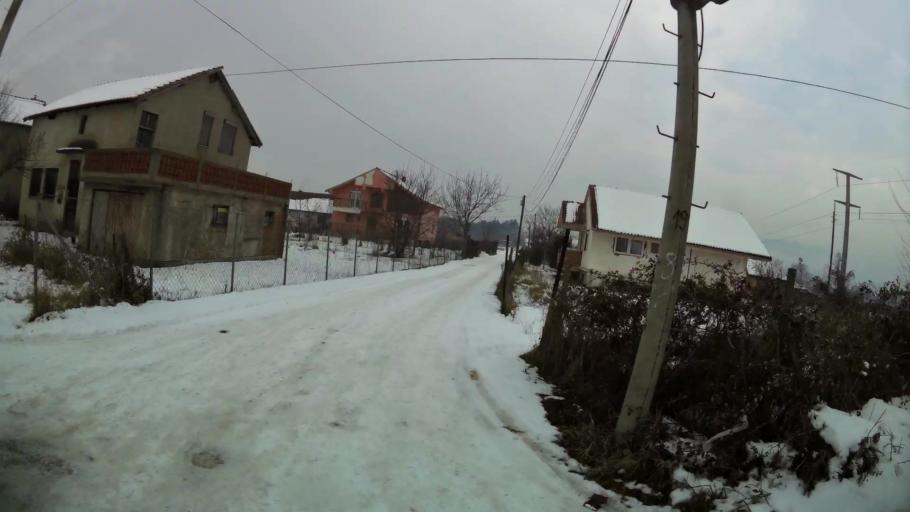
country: MK
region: Saraj
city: Saraj
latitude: 42.0416
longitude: 21.3575
